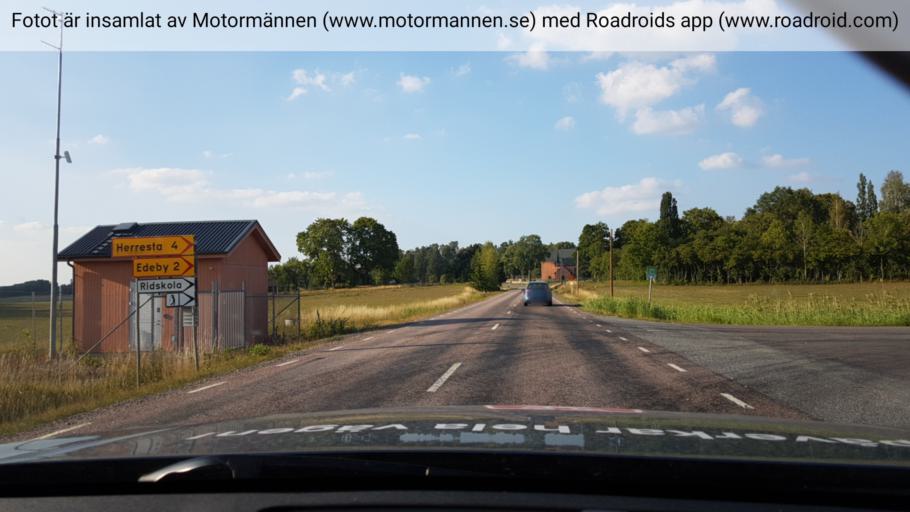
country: SE
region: Soedermanland
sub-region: Strangnas Kommun
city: Stallarholmen
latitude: 59.3395
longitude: 17.2296
